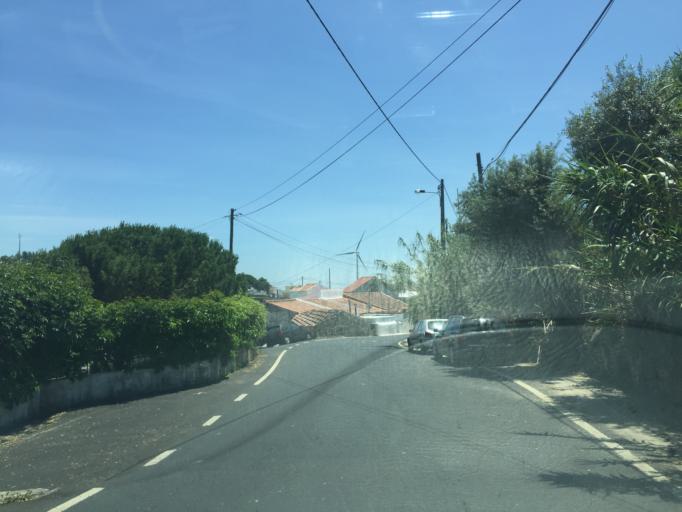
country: PT
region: Lisbon
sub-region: Mafra
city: Venda do Pinheiro
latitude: 38.8882
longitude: -9.2257
